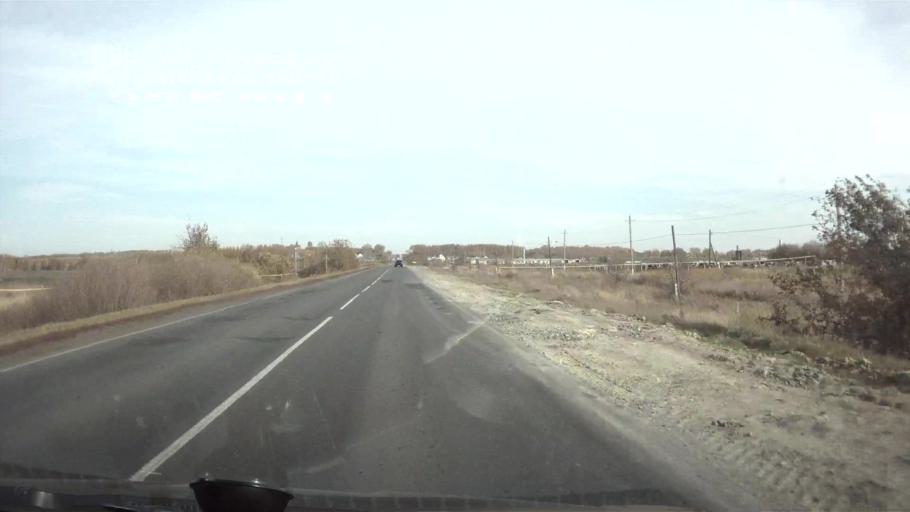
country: RU
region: Mordoviya
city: Atyashevo
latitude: 54.5570
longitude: 45.9691
